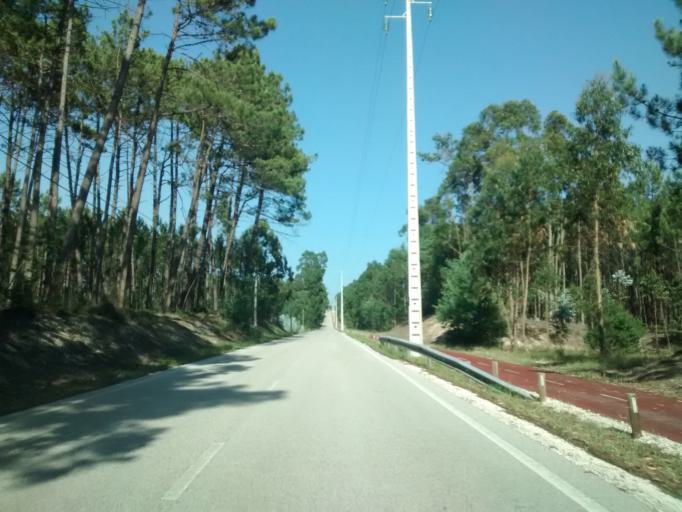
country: PT
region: Leiria
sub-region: Leiria
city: Monte Redondo
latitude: 39.9798
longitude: -8.8237
